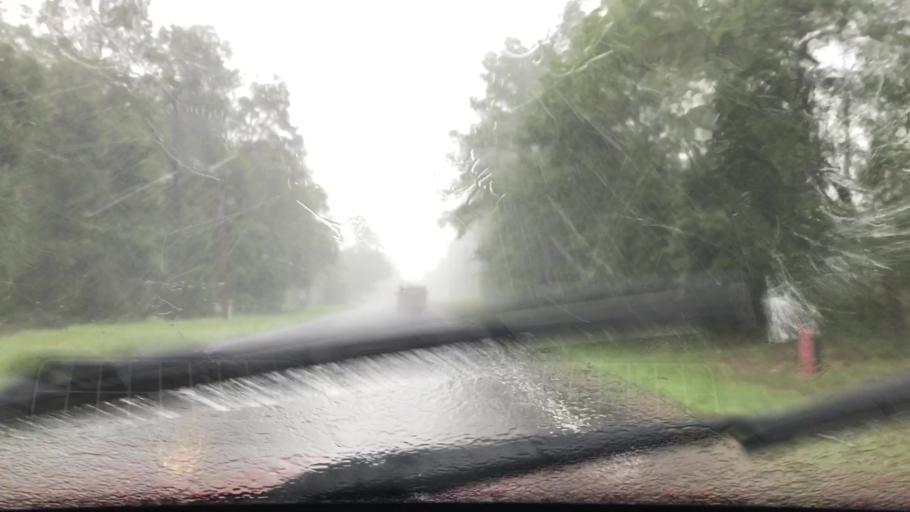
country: US
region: South Carolina
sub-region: Horry County
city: Red Hill
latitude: 33.9034
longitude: -78.9048
